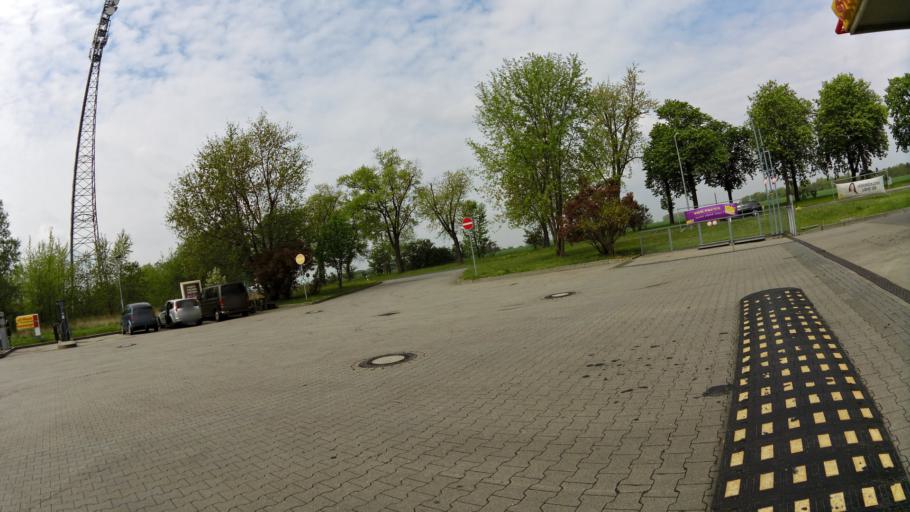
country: DE
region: Brandenburg
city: Mittenwalde
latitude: 52.2633
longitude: 13.5715
